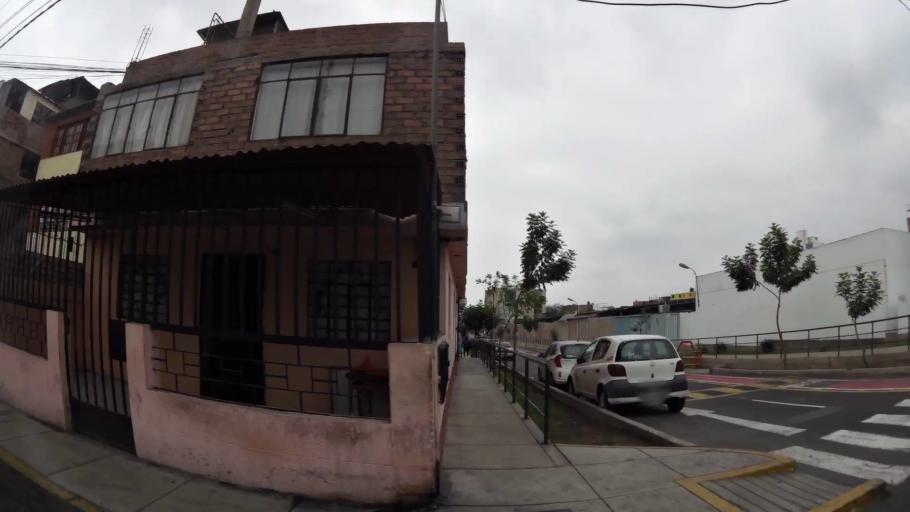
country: PE
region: Lima
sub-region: Lima
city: Surco
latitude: -12.1447
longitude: -77.0055
